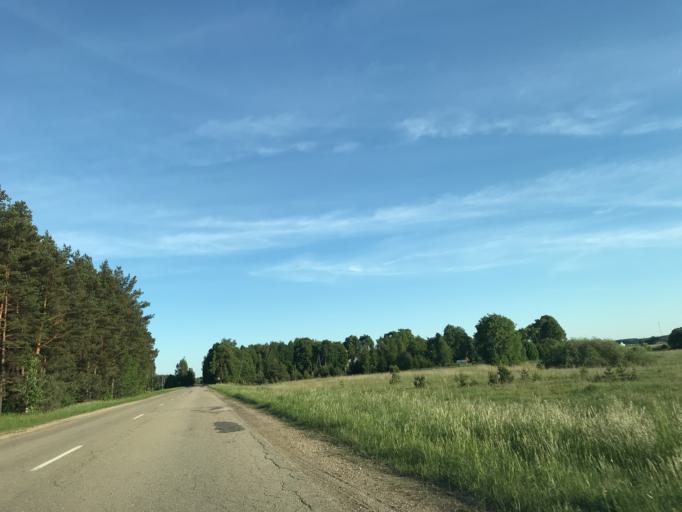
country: LV
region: Ozolnieku
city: Ozolnieki
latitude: 56.6141
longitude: 23.9387
